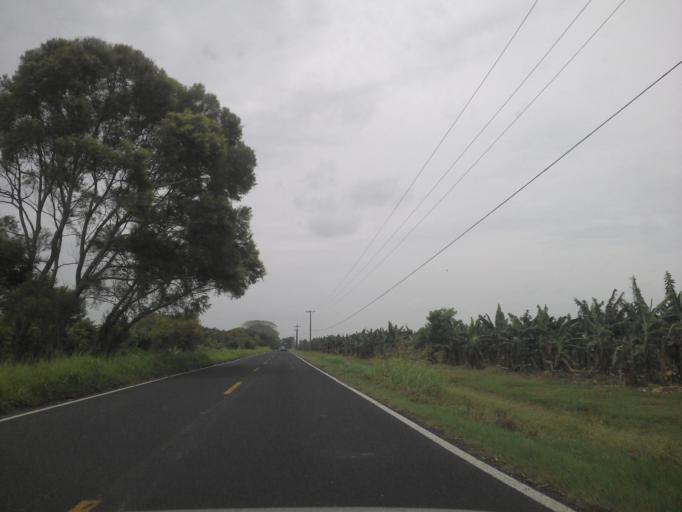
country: MX
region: Veracruz
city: Nautla
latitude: 20.2235
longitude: -96.7869
